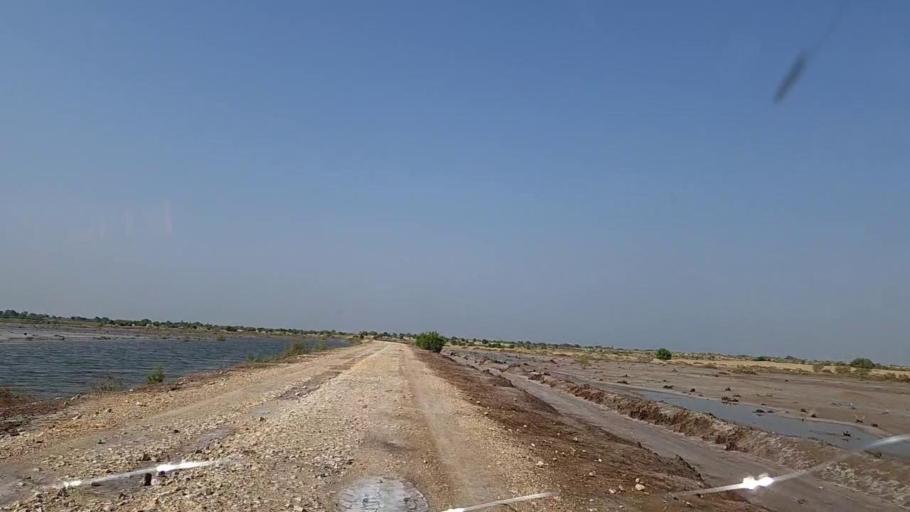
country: PK
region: Sindh
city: Khanpur
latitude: 27.6929
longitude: 69.3833
